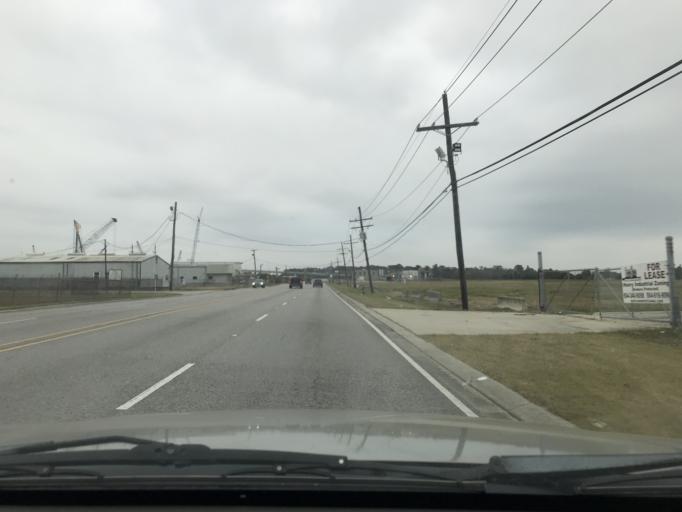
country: US
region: Louisiana
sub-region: Jefferson Parish
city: Woodmere
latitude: 29.8771
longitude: -90.0743
